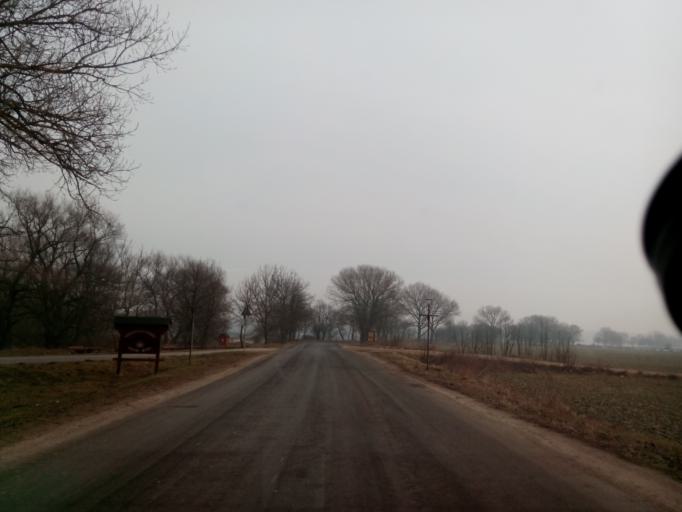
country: HU
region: Borsod-Abauj-Zemplen
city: Gonc
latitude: 48.4967
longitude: 21.2320
